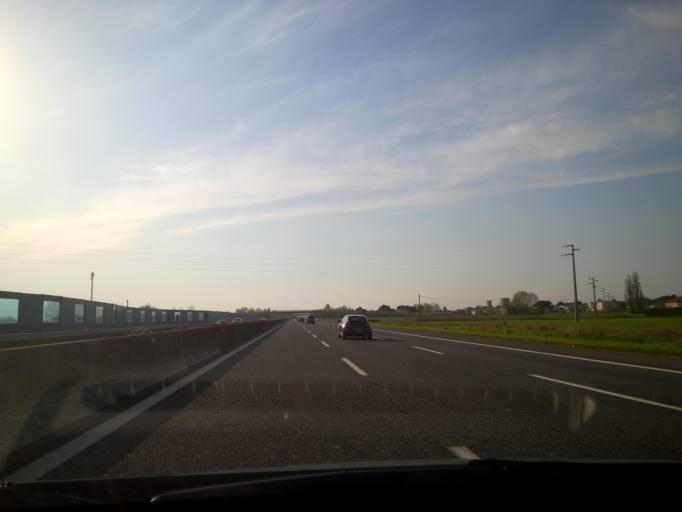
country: IT
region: Emilia-Romagna
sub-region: Provincia di Ravenna
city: Granarolo
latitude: 44.2962
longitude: 11.9735
